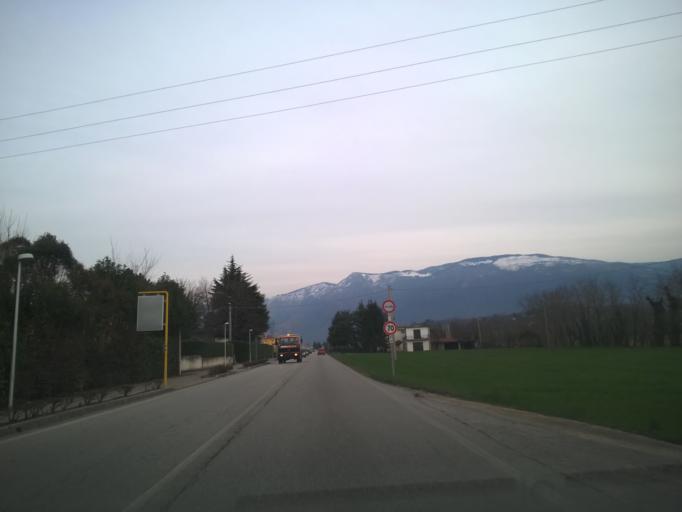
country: IT
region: Veneto
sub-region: Provincia di Vicenza
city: Centrale
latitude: 45.7257
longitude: 11.4665
